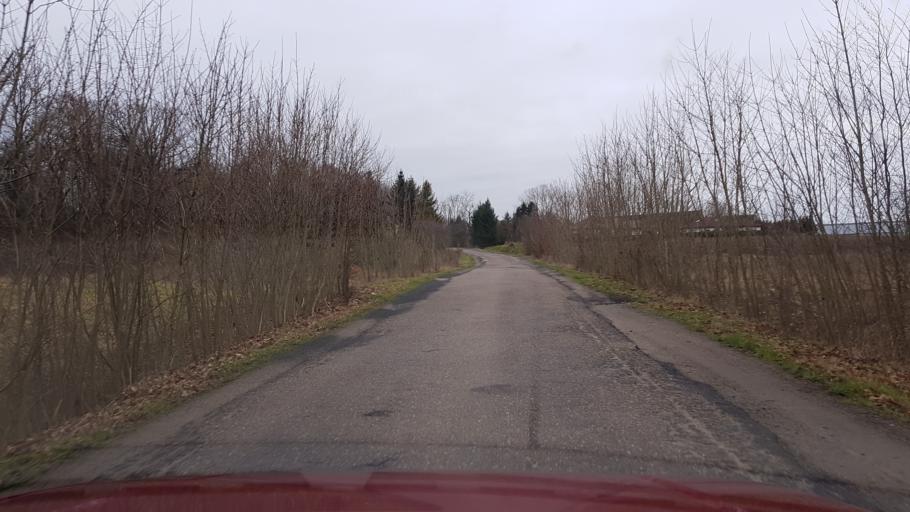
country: PL
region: West Pomeranian Voivodeship
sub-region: Powiat koszalinski
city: Mielno
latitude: 54.1876
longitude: 16.0241
